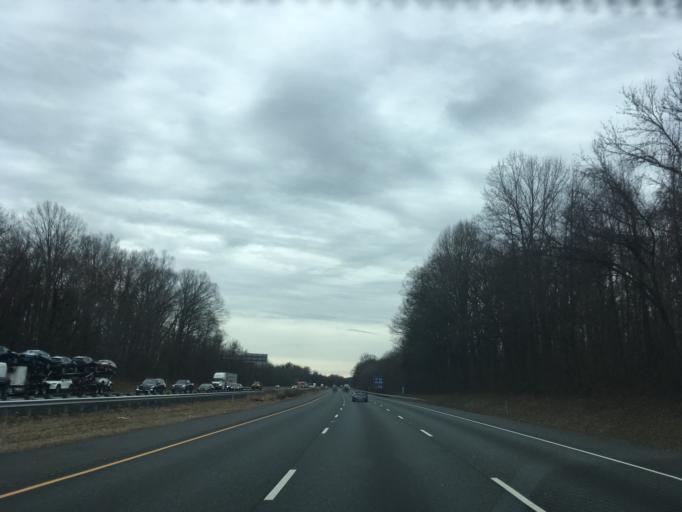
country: US
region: Maryland
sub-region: Harford County
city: Aberdeen
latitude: 39.5433
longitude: -76.1704
